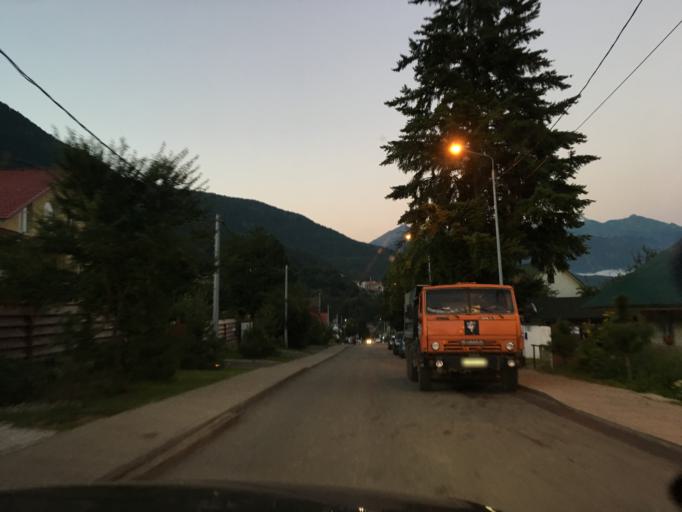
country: RU
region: Krasnodarskiy
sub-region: Sochi City
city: Krasnaya Polyana
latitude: 43.6798
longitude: 40.2075
